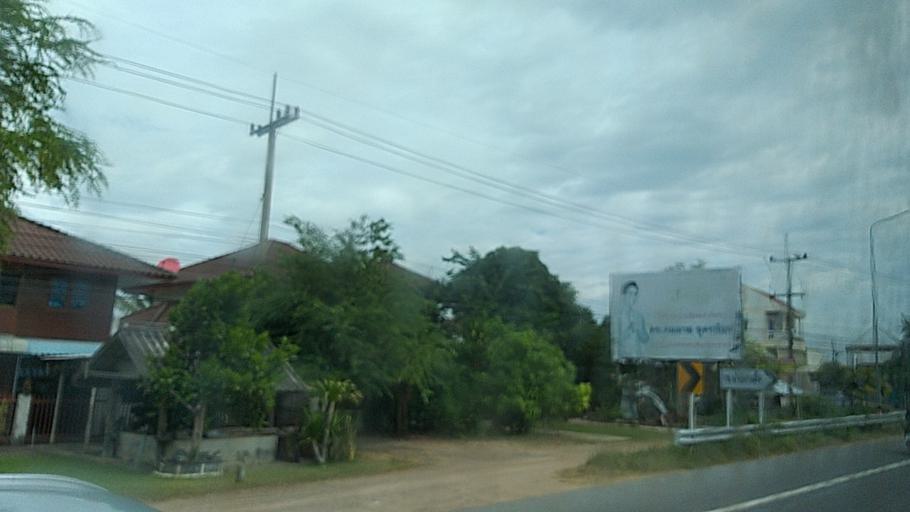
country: TH
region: Maha Sarakham
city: Maha Sarakham
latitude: 16.1572
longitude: 103.3684
